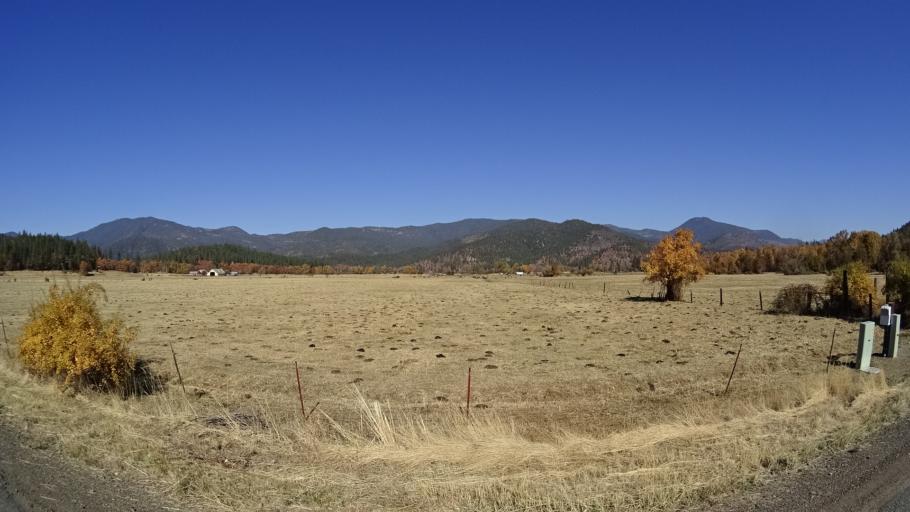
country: US
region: California
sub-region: Siskiyou County
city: Yreka
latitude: 41.6177
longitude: -122.9706
